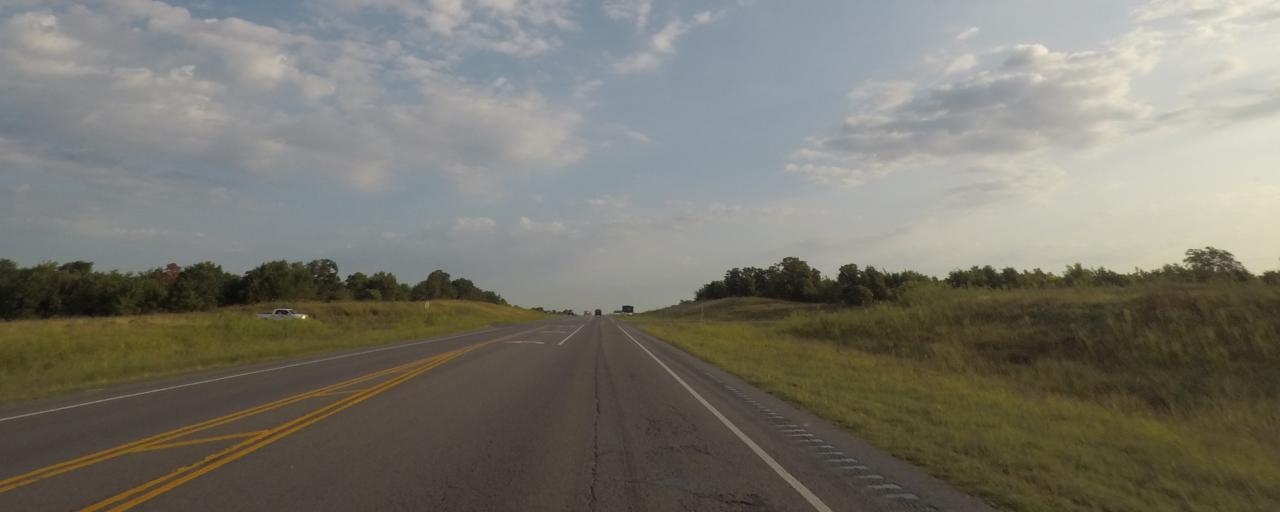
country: US
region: Oklahoma
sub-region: Stephens County
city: Meridian
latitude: 34.4483
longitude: -97.9741
